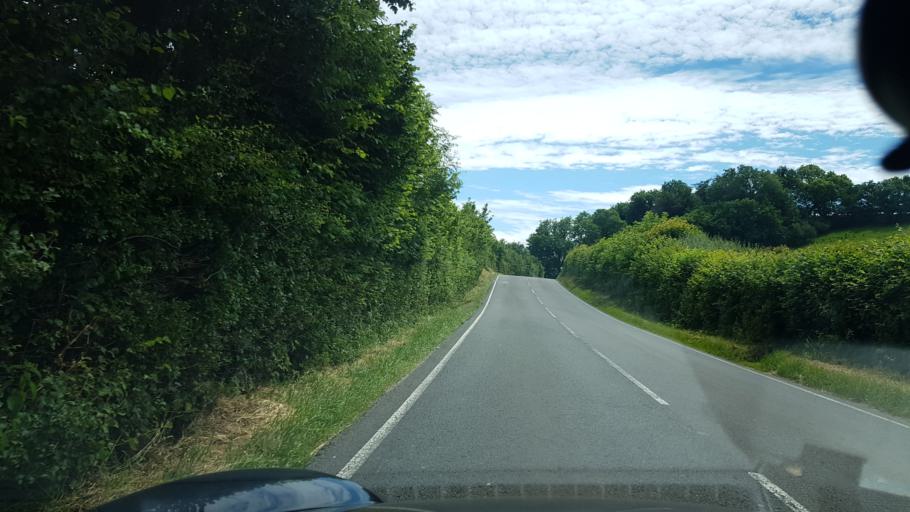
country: GB
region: Wales
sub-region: Carmarthenshire
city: Saint Clears
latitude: 51.8014
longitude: -4.4927
